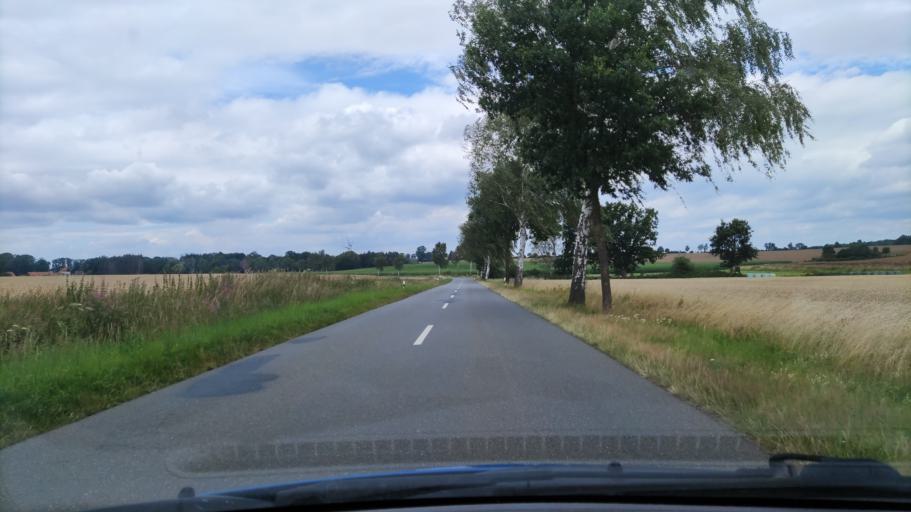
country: DE
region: Lower Saxony
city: Romstedt
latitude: 53.1118
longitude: 10.6484
